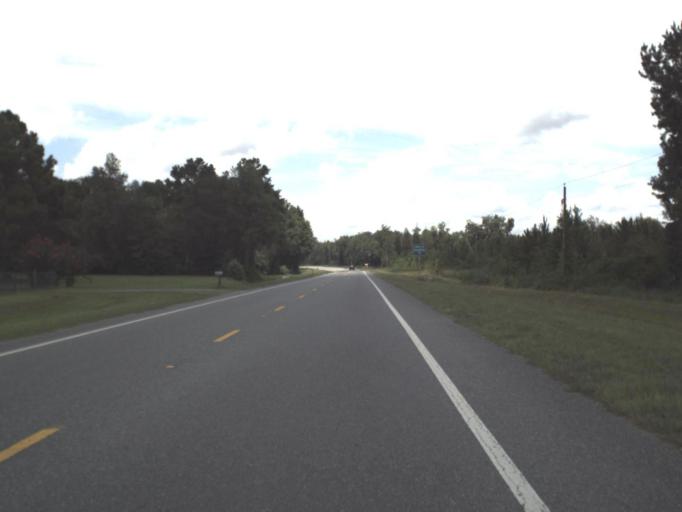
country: US
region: Florida
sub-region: Suwannee County
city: Live Oak
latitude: 30.3597
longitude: -82.9435
